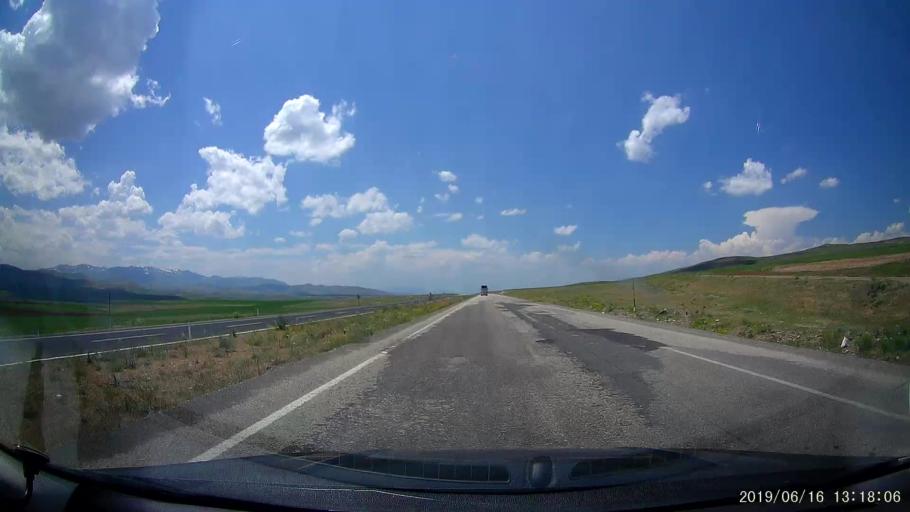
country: TR
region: Agri
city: Taslicay
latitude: 39.6294
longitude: 43.4380
